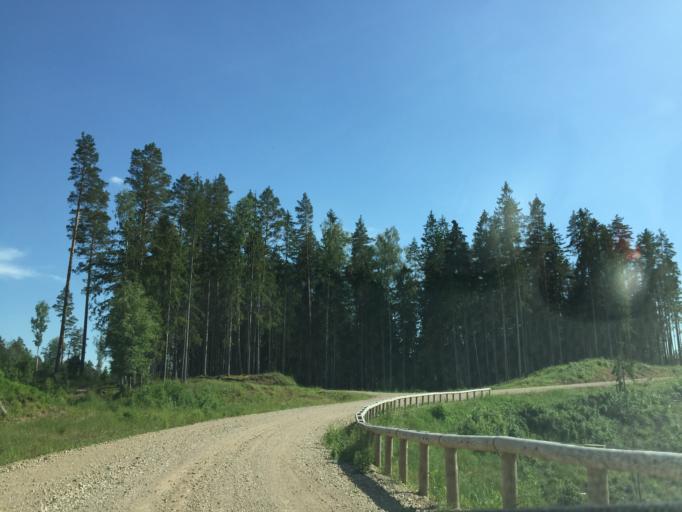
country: LV
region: Tukuma Rajons
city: Tukums
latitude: 57.0183
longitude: 23.2264
